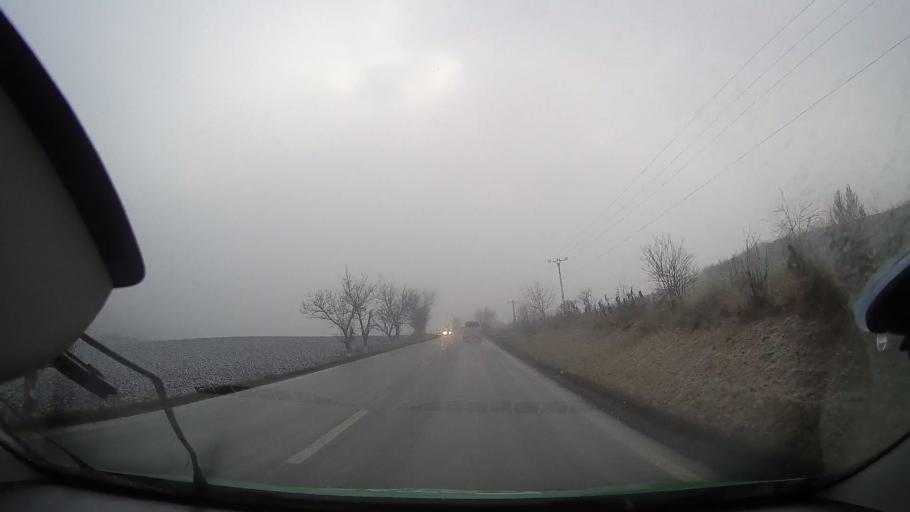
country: RO
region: Mures
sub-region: Municipiul Tarnaveni
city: Tarnaveni
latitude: 46.2929
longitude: 24.3014
